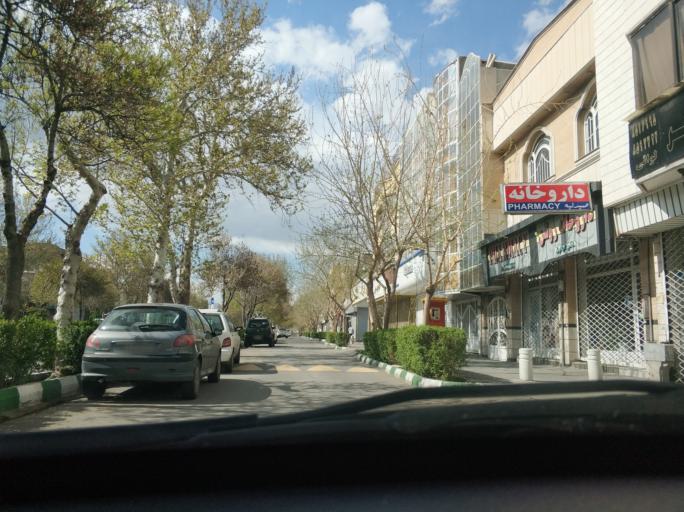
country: IR
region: Razavi Khorasan
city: Mashhad
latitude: 36.2717
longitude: 59.5953
